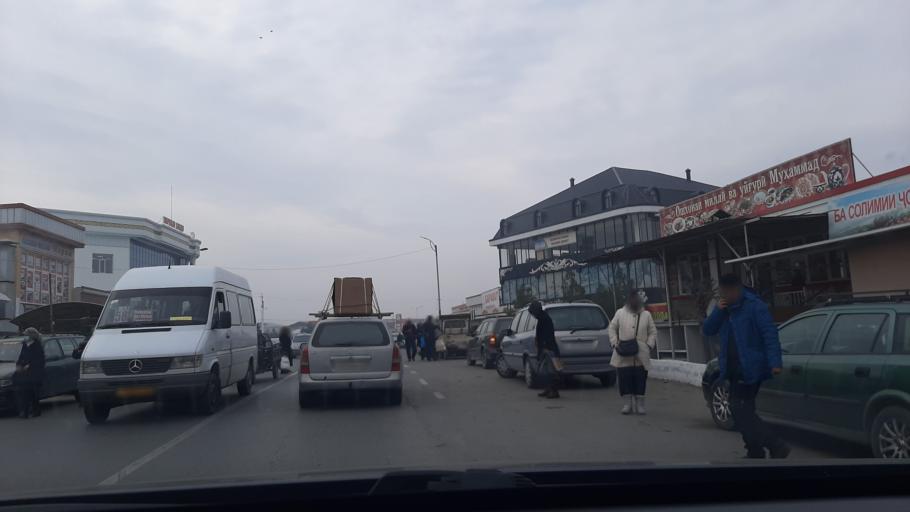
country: TJ
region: Viloyati Sughd
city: Chkalov
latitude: 40.2456
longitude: 69.7016
